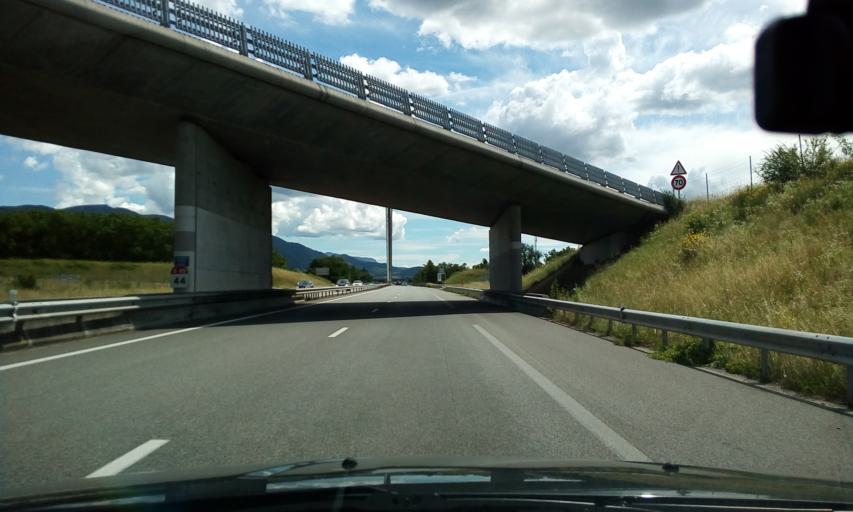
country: FR
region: Rhone-Alpes
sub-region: Departement de l'Isere
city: Saint-Lattier
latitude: 45.0865
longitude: 5.2166
